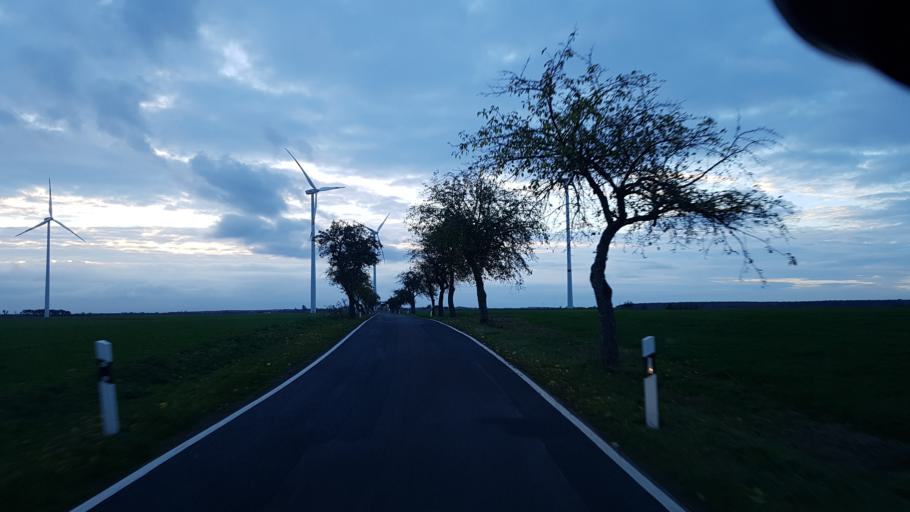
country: DE
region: Brandenburg
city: Muhlberg
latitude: 51.4726
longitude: 13.2401
